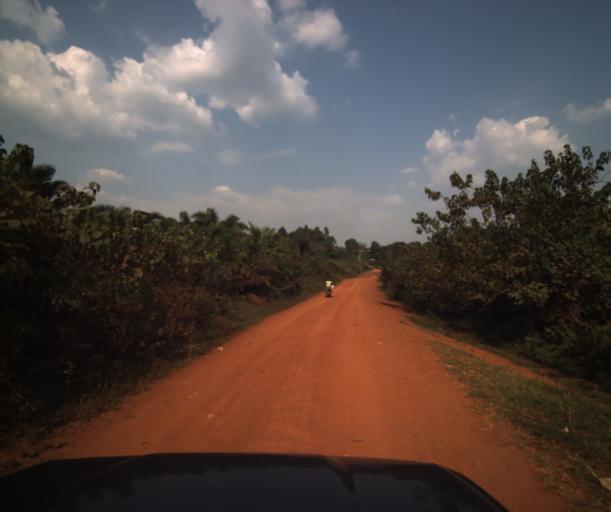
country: CM
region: Centre
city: Akono
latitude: 3.5936
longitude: 11.3005
